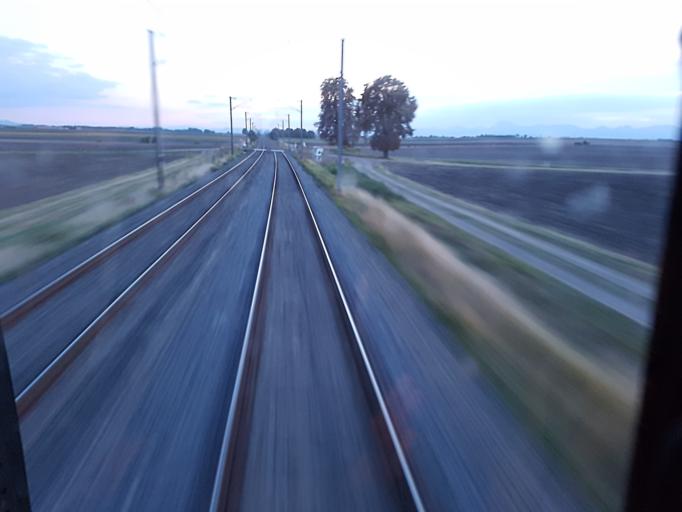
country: FR
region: Auvergne
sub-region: Departement du Puy-de-Dome
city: Ennezat
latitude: 45.9519
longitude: 3.2468
